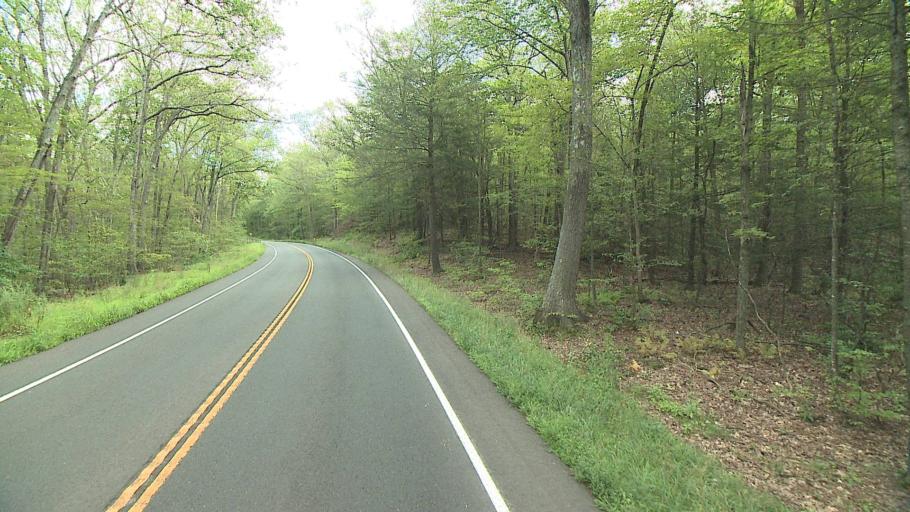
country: US
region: Connecticut
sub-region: Tolland County
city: Ellington
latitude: 41.9128
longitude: -72.4366
